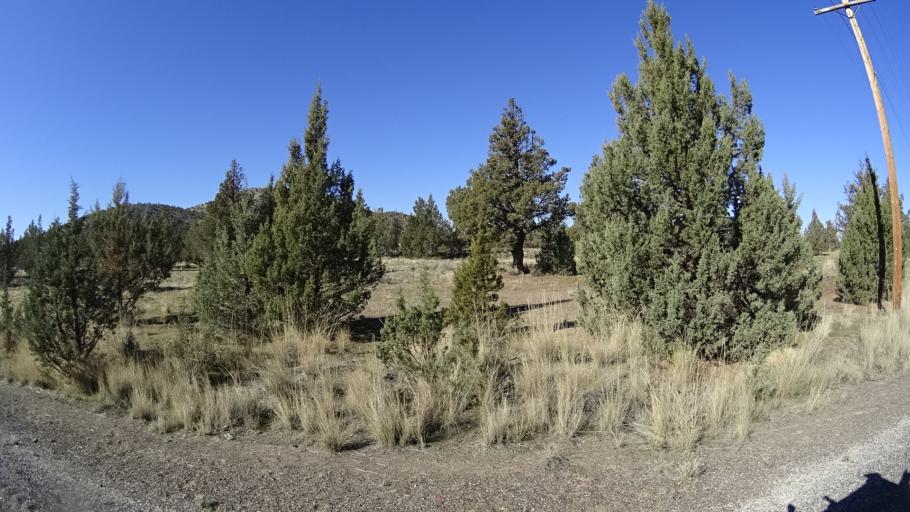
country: US
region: California
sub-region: Siskiyou County
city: Montague
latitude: 41.6718
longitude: -122.3698
